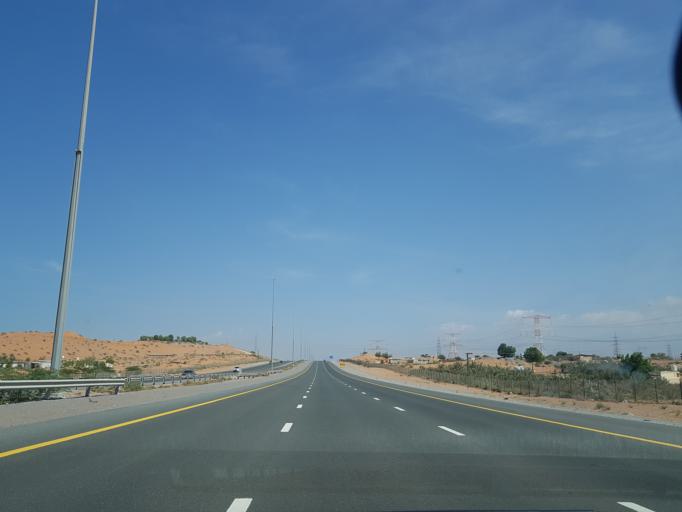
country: AE
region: Ra's al Khaymah
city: Ras al-Khaimah
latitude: 25.6862
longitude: 55.9137
